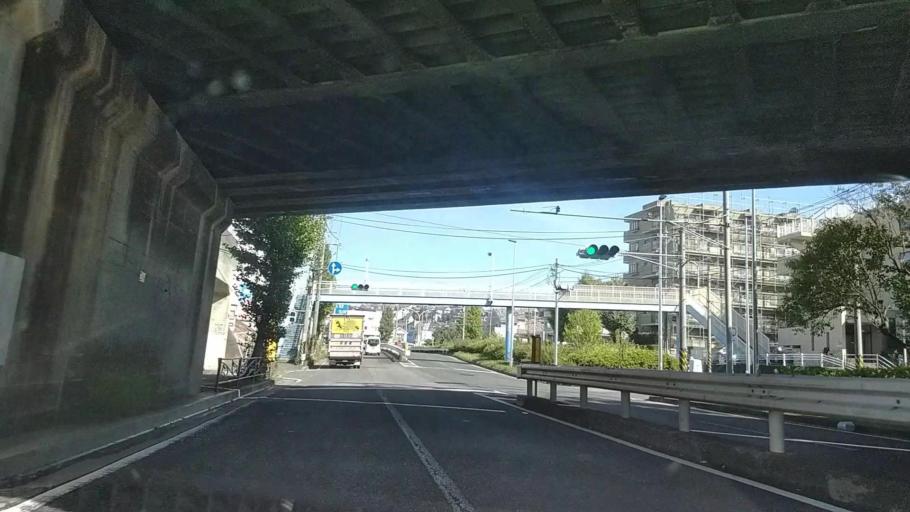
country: JP
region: Tokyo
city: Chofugaoka
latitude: 35.5788
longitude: 139.6112
